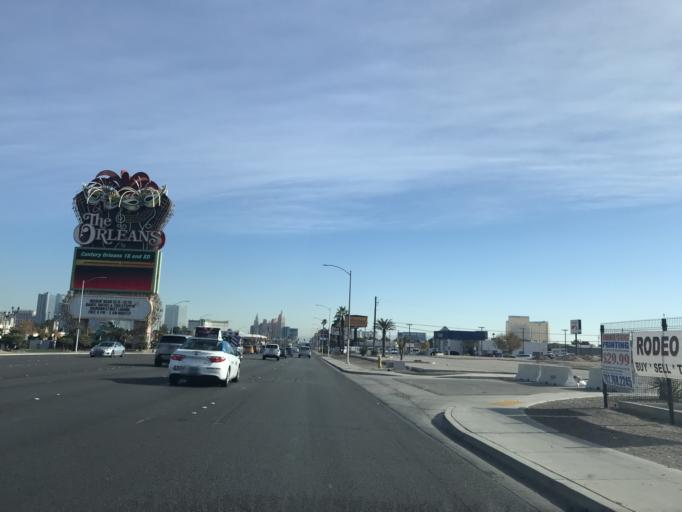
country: US
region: Nevada
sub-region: Clark County
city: Spring Valley
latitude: 36.1008
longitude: -115.2032
